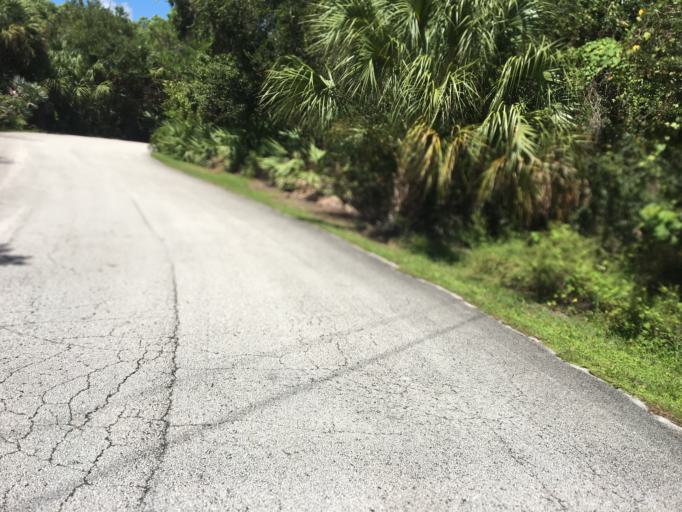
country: US
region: Florida
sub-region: Martin County
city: Palm City
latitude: 27.1867
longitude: -80.2699
